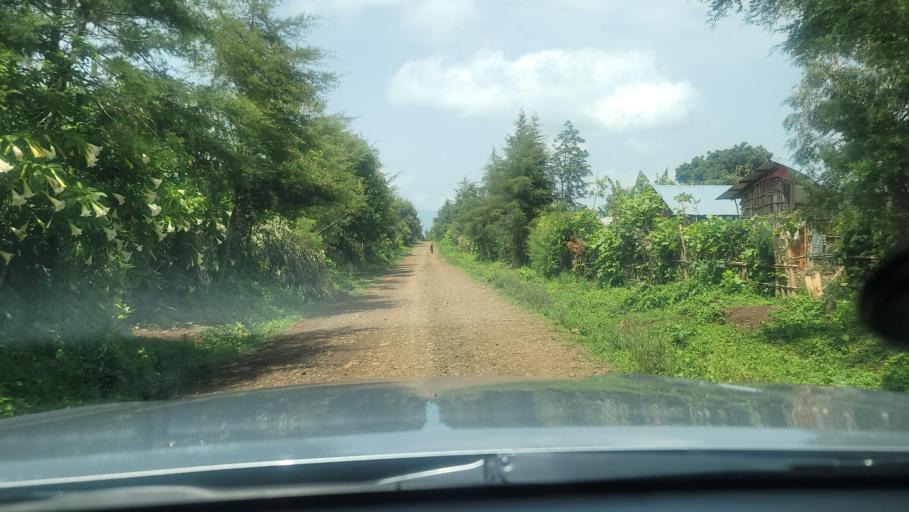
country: ET
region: Oromiya
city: Agaro
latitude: 7.8233
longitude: 36.4080
